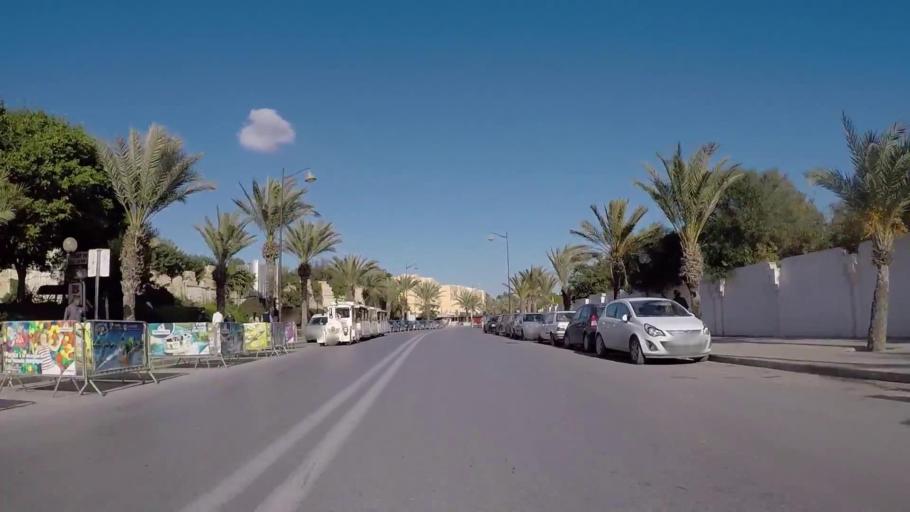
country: TN
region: Nabul
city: Al Hammamat
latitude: 36.3673
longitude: 10.5348
